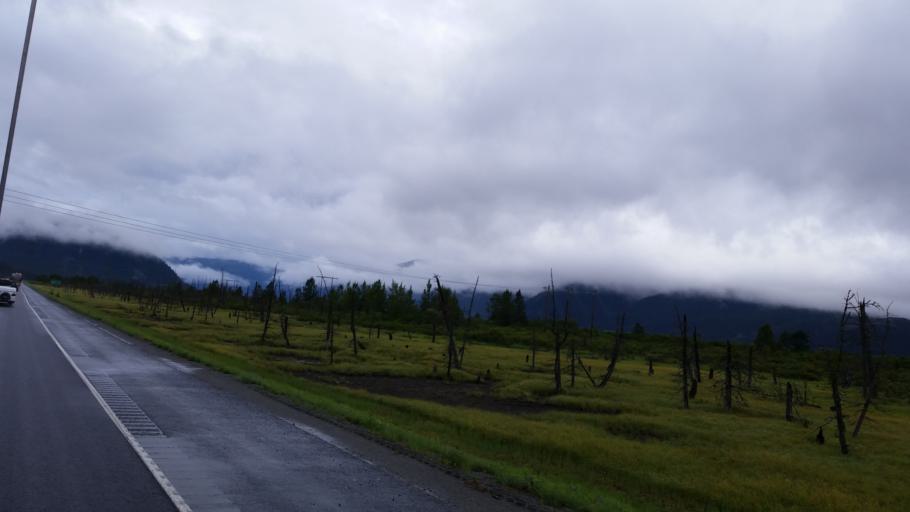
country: US
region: Alaska
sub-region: Anchorage Municipality
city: Girdwood
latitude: 60.8212
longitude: -149.0038
